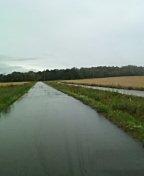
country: SE
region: Vaestmanland
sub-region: Kopings Kommun
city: Koping
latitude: 59.4948
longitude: 16.0303
